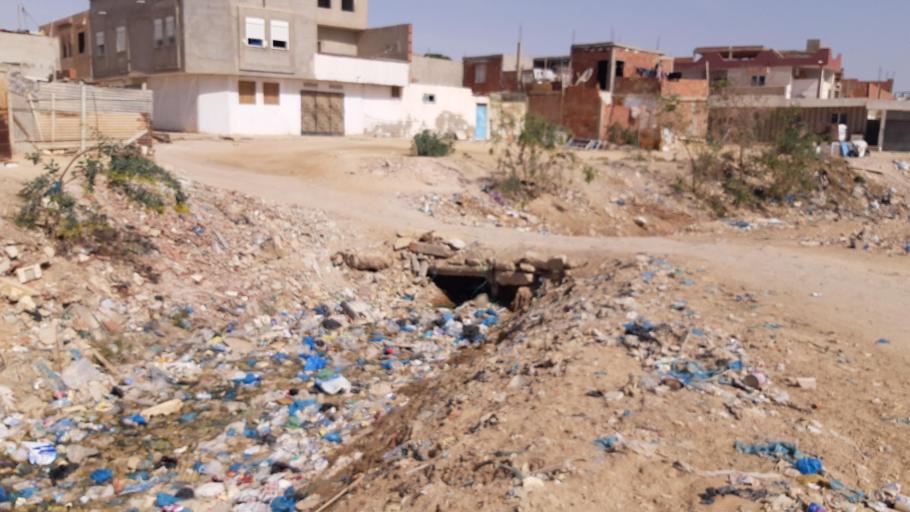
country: TN
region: Qabis
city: Gabes
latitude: 33.8623
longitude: 10.0817
